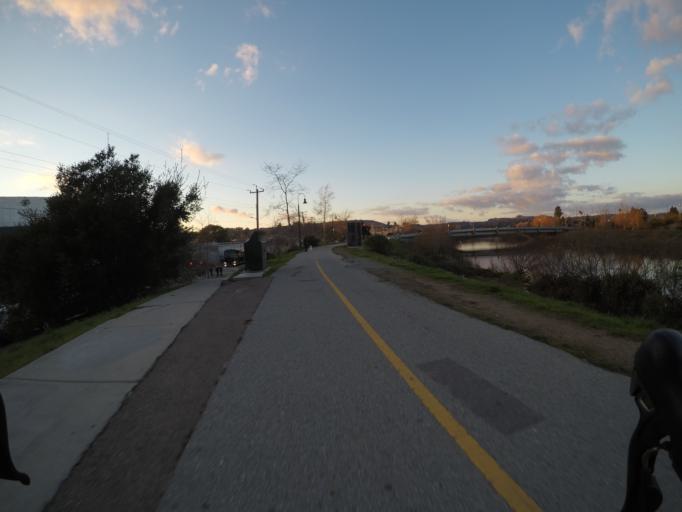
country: US
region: California
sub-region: Santa Cruz County
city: Santa Cruz
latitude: 36.9684
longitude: -122.0224
